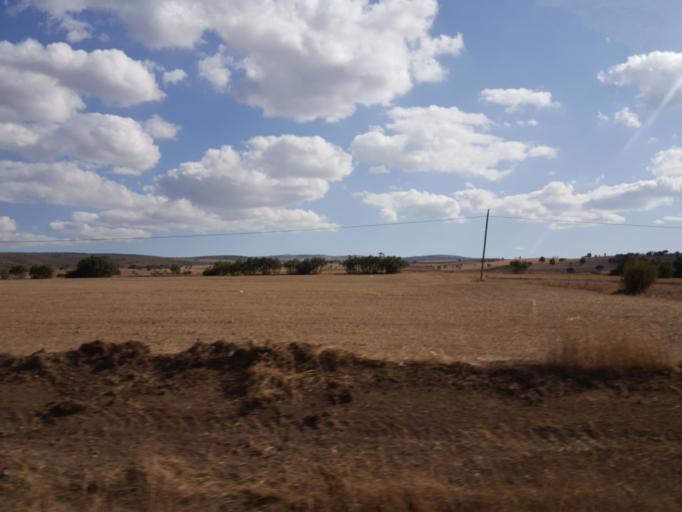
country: TR
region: Tokat
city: Sulusaray
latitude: 40.0025
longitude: 36.1333
